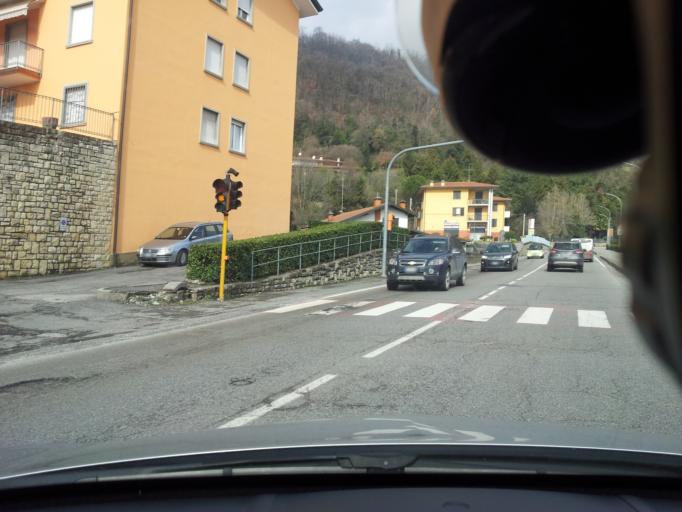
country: IT
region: Lombardy
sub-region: Provincia di Bergamo
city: Tagliuno
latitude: 45.6479
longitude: 9.9095
